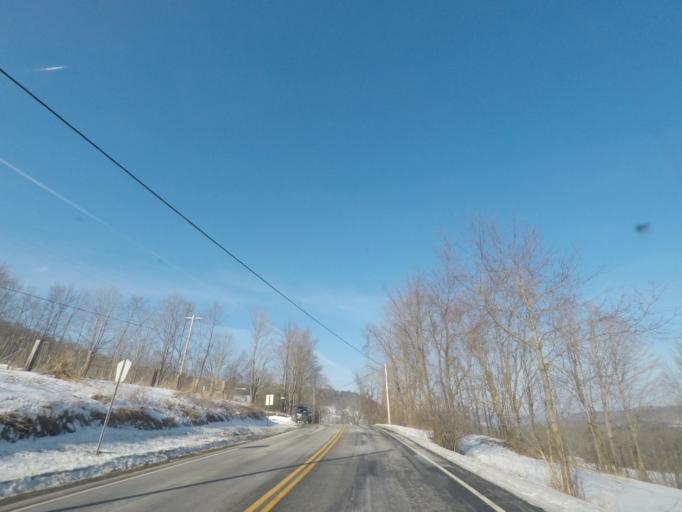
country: US
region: Massachusetts
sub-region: Berkshire County
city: Richmond
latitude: 42.4910
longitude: -73.3874
